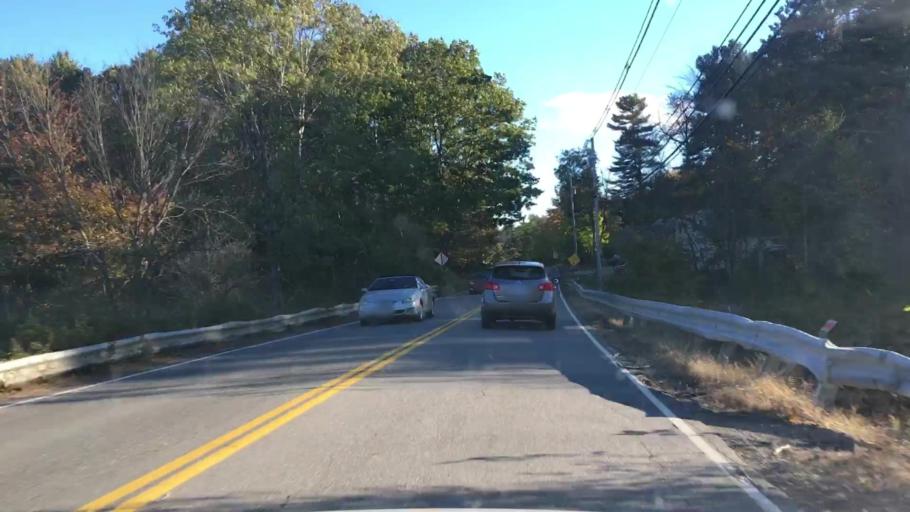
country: US
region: Maine
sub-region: Cumberland County
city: South Portland Gardens
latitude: 43.6144
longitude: -70.3413
